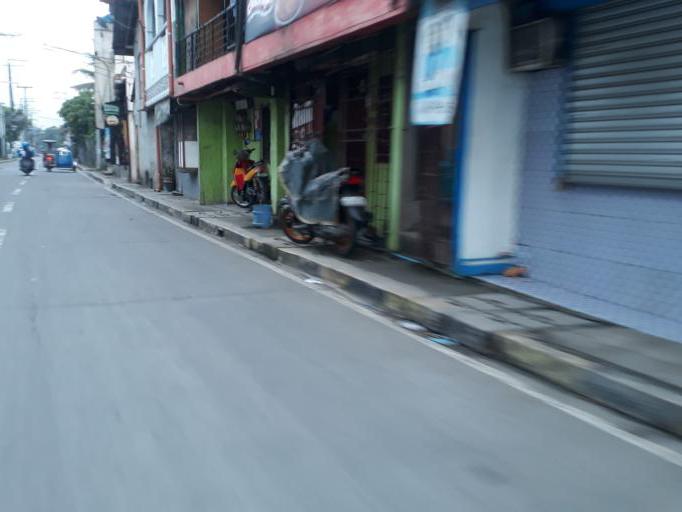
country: PH
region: Calabarzon
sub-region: Province of Rizal
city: Valenzuela
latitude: 14.7027
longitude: 120.9558
